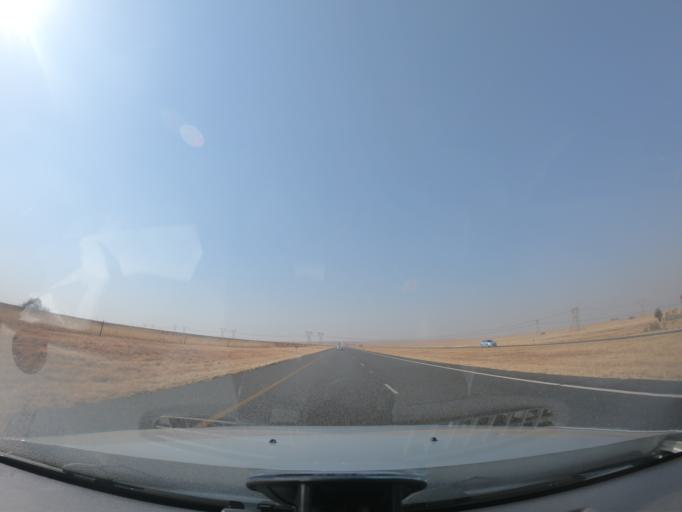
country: ZA
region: Gauteng
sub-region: City of Tshwane Metropolitan Municipality
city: Bronkhorstspruit
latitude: -25.8600
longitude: 28.8901
